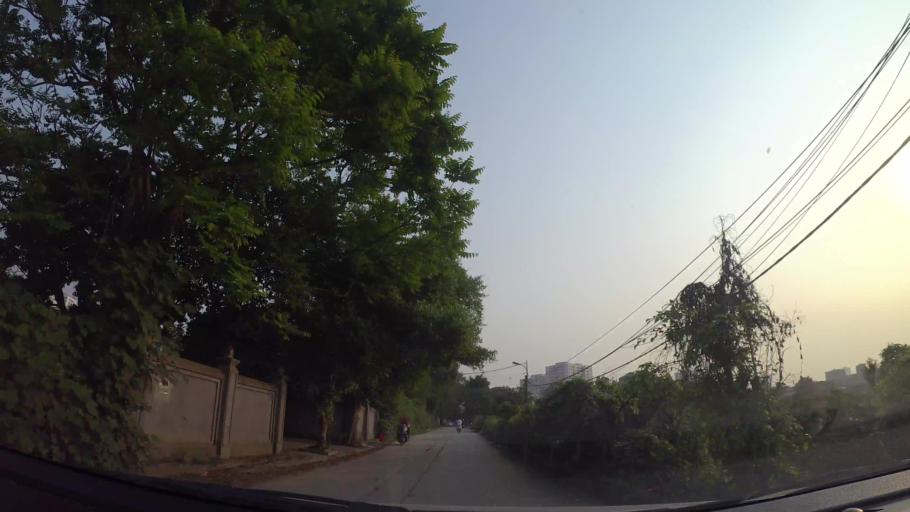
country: VN
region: Ha Noi
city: Tay Ho
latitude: 21.0737
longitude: 105.7946
